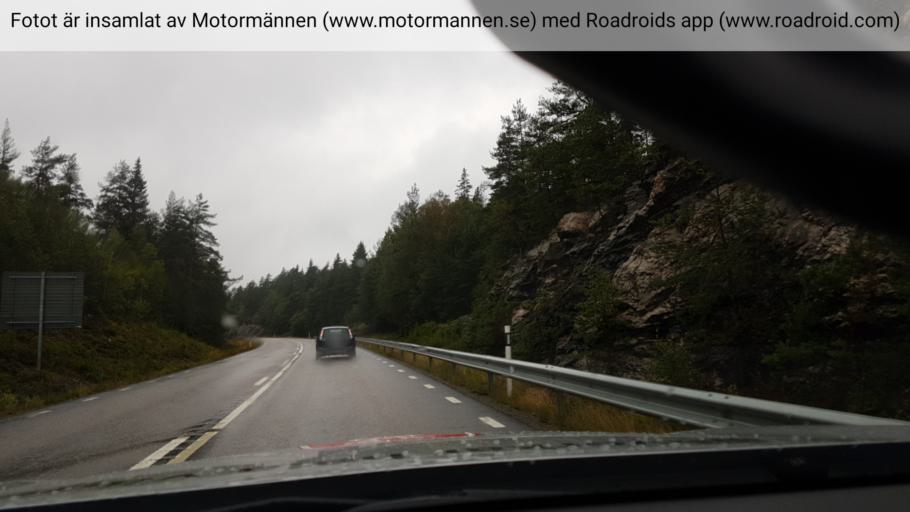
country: SE
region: Vaestra Goetaland
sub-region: Dals-Ed Kommun
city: Ed
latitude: 58.8752
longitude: 11.8562
